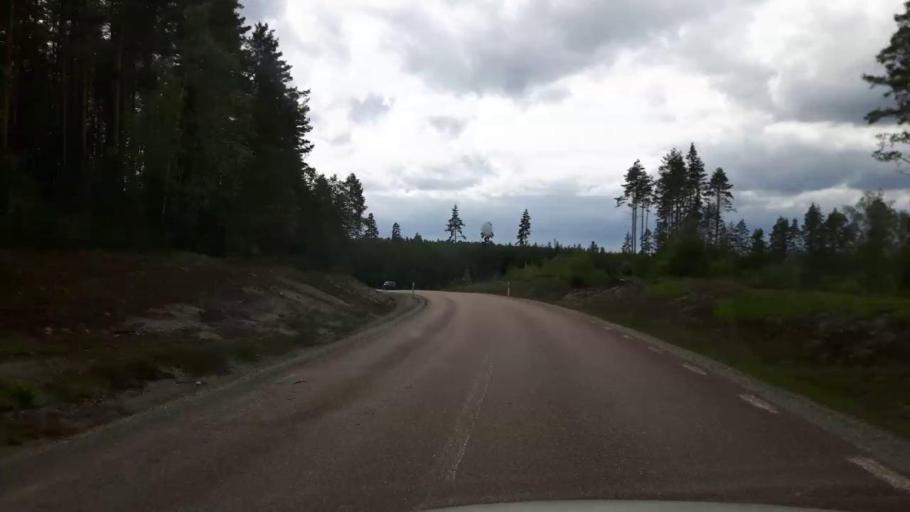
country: SE
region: Vaestmanland
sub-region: Skinnskattebergs Kommun
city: Skinnskatteberg
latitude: 59.8329
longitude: 15.8347
